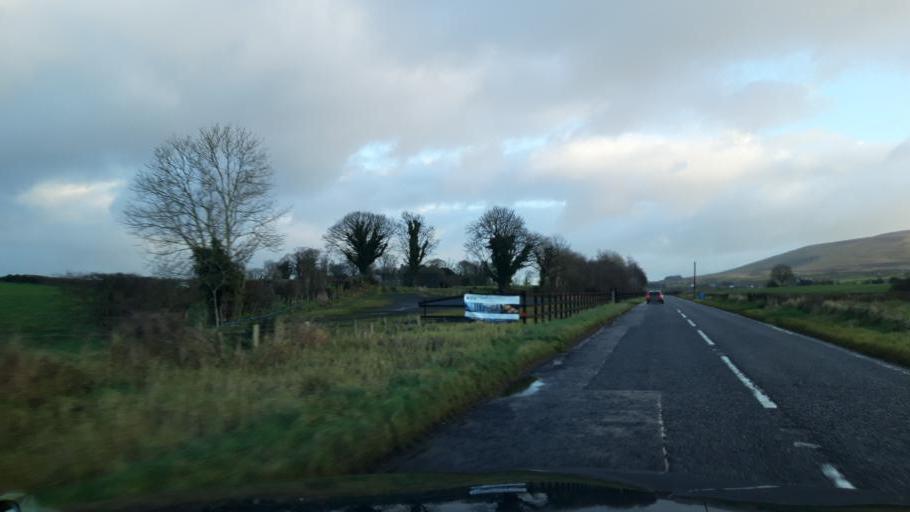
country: GB
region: Northern Ireland
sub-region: Moyle District
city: Ballycastle
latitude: 55.1396
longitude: -6.3238
